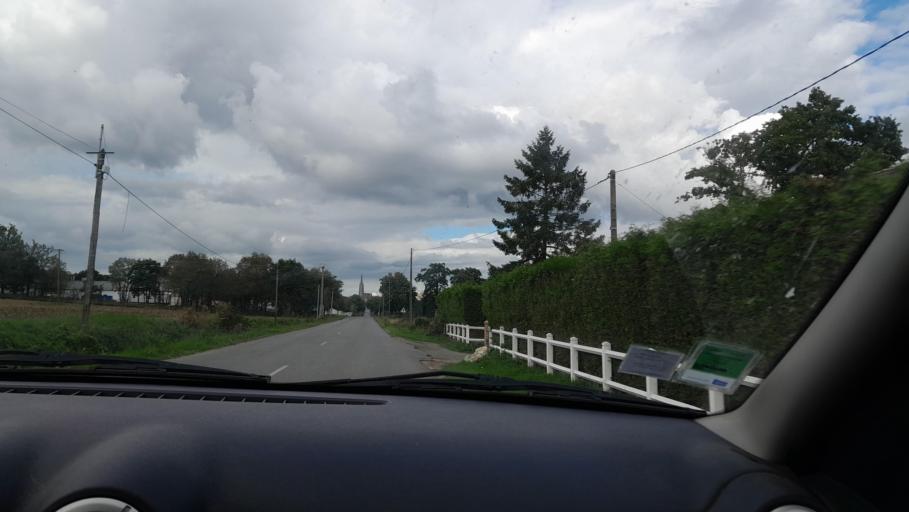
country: FR
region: Brittany
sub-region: Departement d'Ille-et-Vilaine
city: Le Pertre
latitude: 48.0186
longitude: -1.0376
